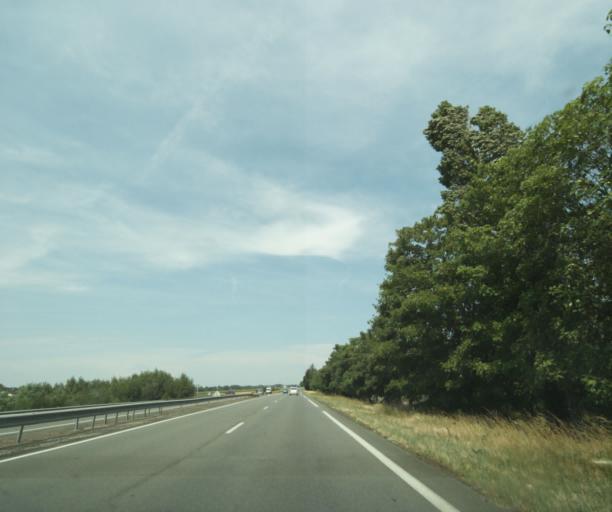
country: FR
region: Poitou-Charentes
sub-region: Departement de la Vienne
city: Dange-Saint-Romain
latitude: 46.8985
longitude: 0.5728
